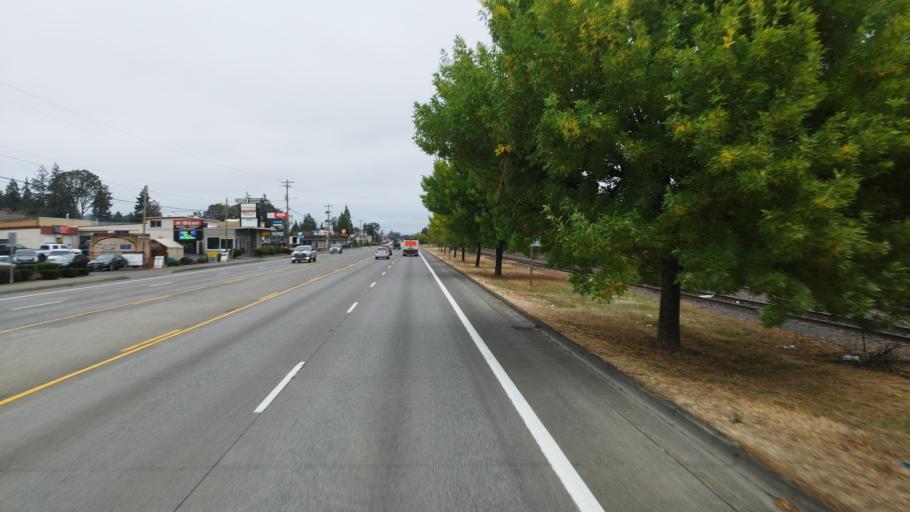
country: US
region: Oregon
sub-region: Columbia County
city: Saint Helens
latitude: 45.8513
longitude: -122.8288
